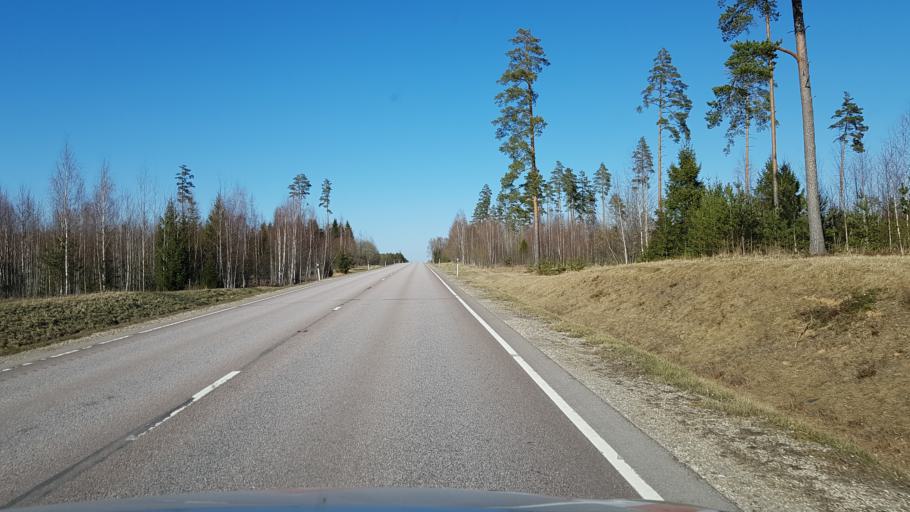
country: EE
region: Jogevamaa
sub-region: Mustvee linn
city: Mustvee
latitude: 58.7379
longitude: 26.8485
